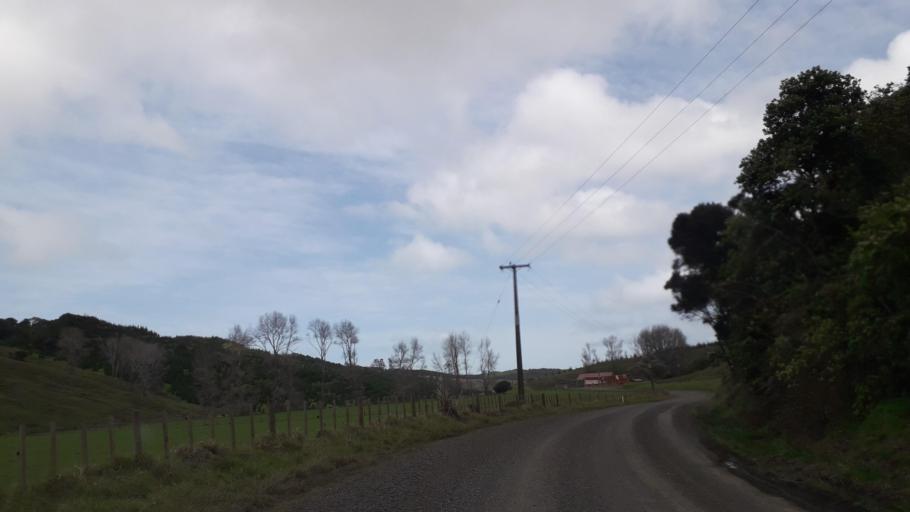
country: NZ
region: Northland
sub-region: Far North District
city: Ahipara
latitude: -35.4232
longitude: 173.3595
